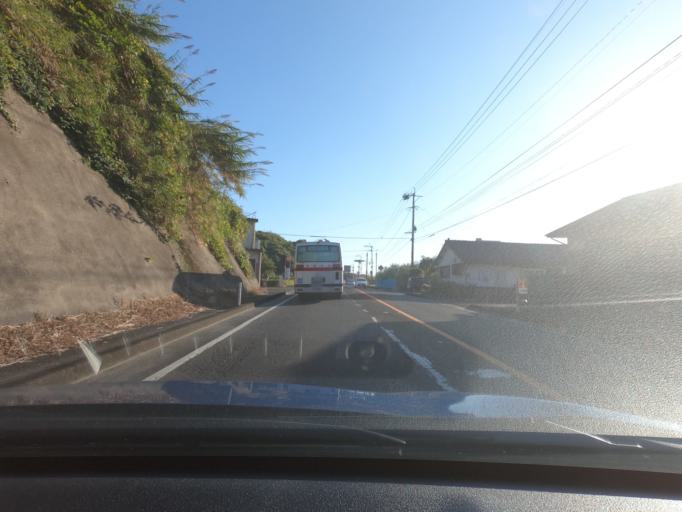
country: JP
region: Kagoshima
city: Akune
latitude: 31.9846
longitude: 130.2038
